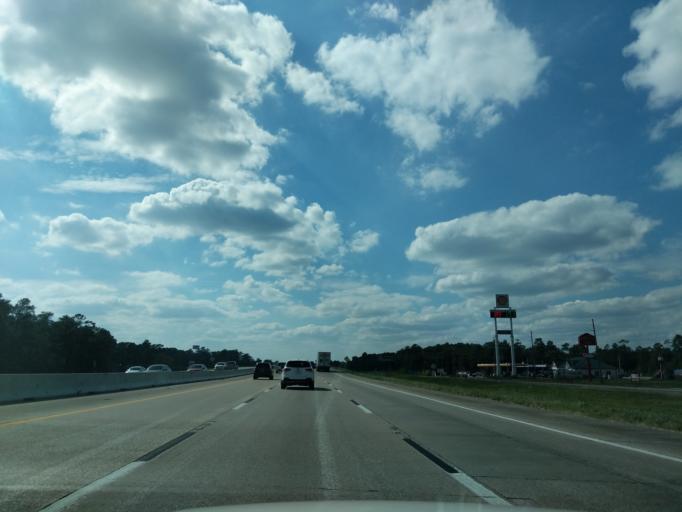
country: US
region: Texas
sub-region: Chambers County
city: Anahuac
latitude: 29.8404
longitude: -94.6446
